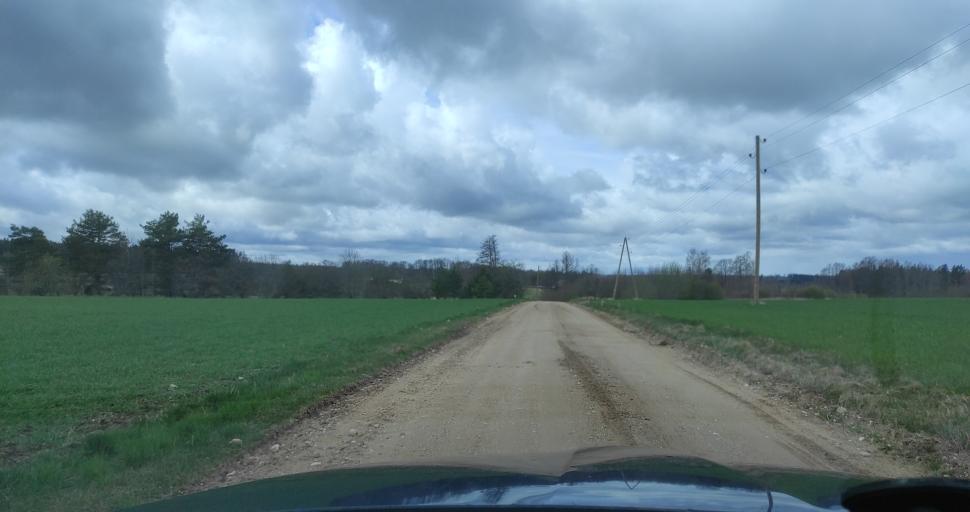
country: LV
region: Ventspils Rajons
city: Piltene
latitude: 57.0570
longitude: 21.7753
